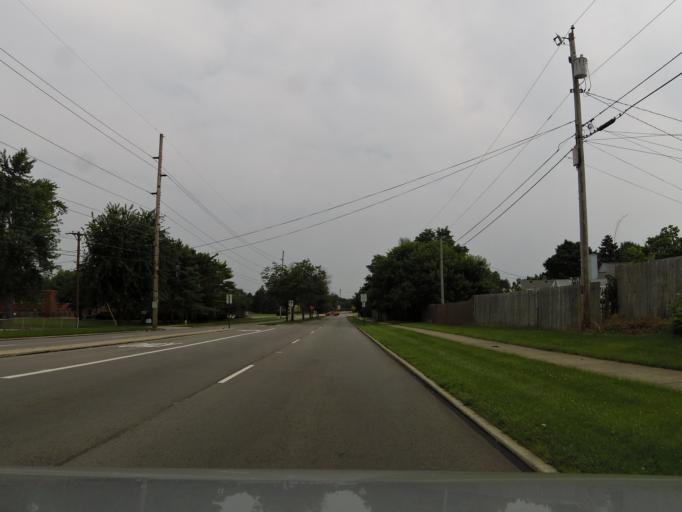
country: US
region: Ohio
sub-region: Montgomery County
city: Oakwood
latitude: 39.7191
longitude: -84.1243
